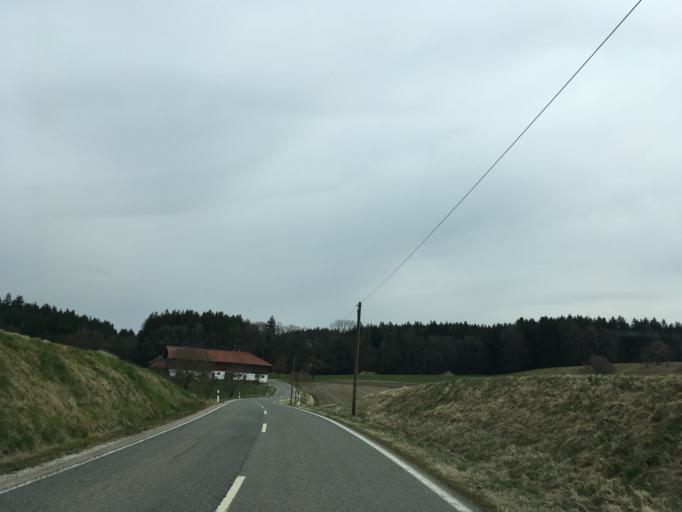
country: DE
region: Bavaria
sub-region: Upper Bavaria
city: Amerang
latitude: 48.0134
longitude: 12.3484
